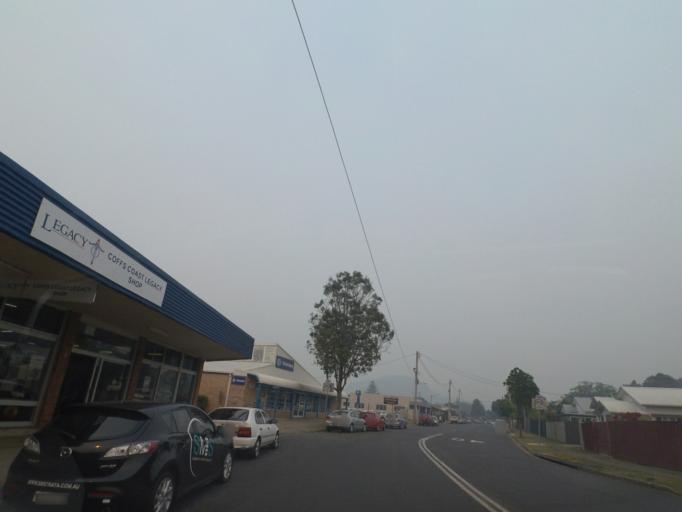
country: AU
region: New South Wales
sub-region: Coffs Harbour
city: Coffs Harbour
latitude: -30.2946
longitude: 153.1129
